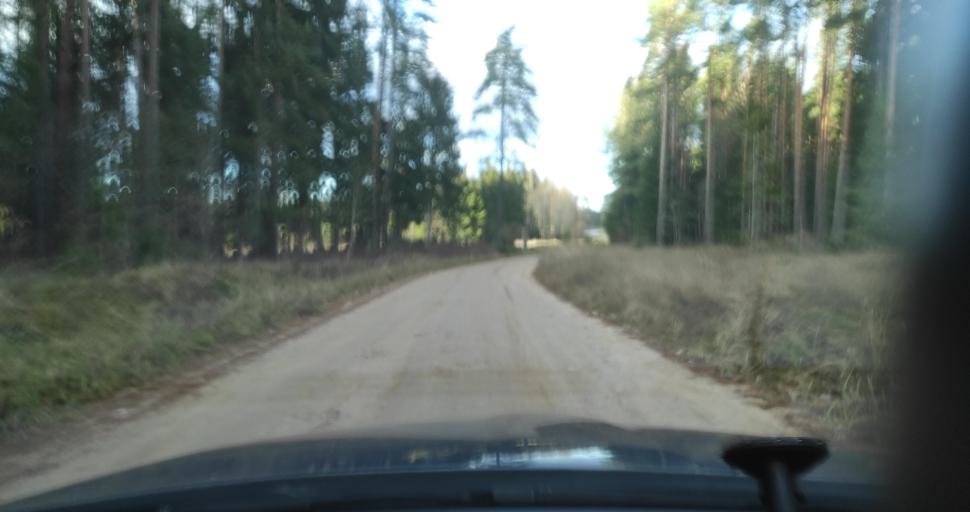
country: LV
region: Kuldigas Rajons
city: Kuldiga
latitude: 57.2852
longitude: 22.0389
